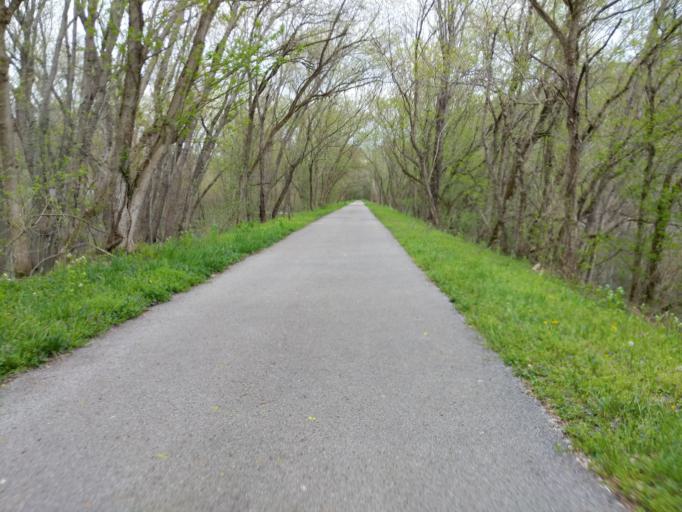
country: US
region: Ohio
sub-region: Athens County
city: Chauncey
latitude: 39.3877
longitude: -82.1245
